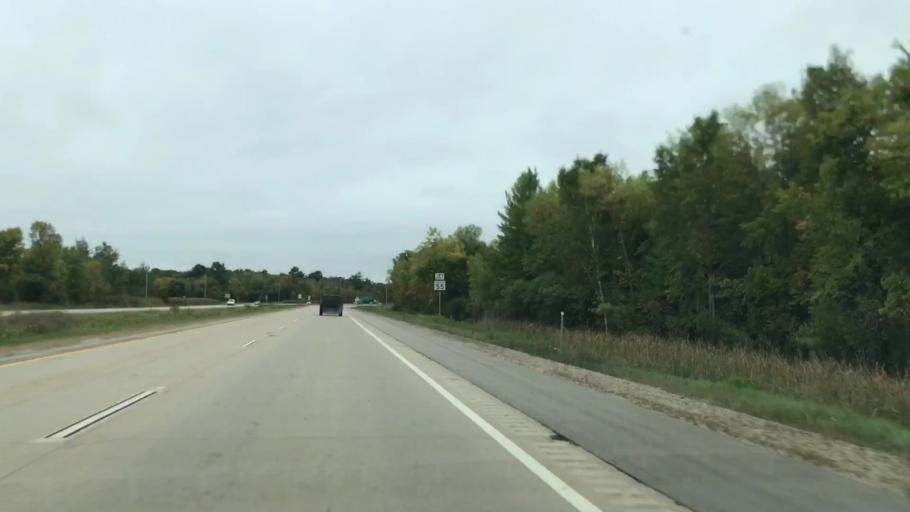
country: US
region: Wisconsin
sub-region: Oconto County
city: Oconto
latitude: 44.8191
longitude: -87.9416
